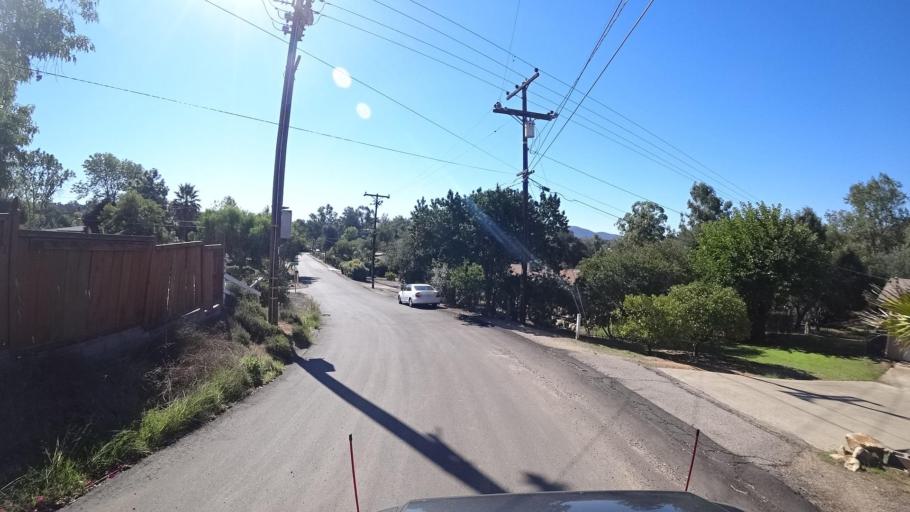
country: US
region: California
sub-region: San Diego County
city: Jamul
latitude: 32.7254
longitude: -116.8731
